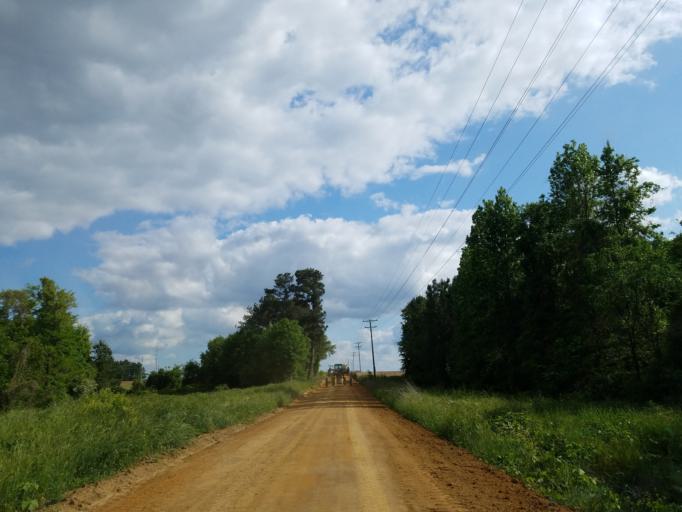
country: US
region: Georgia
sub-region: Dooly County
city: Vienna
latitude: 32.1484
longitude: -83.7859
